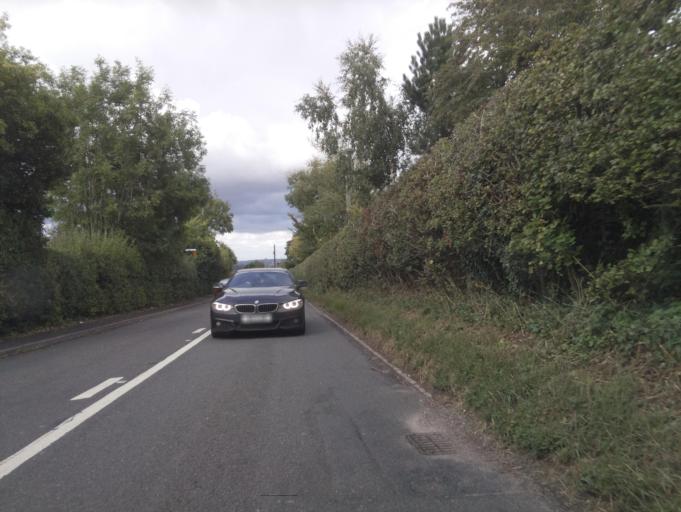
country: GB
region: England
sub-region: Staffordshire
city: Eccleshall
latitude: 52.8529
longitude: -2.2531
